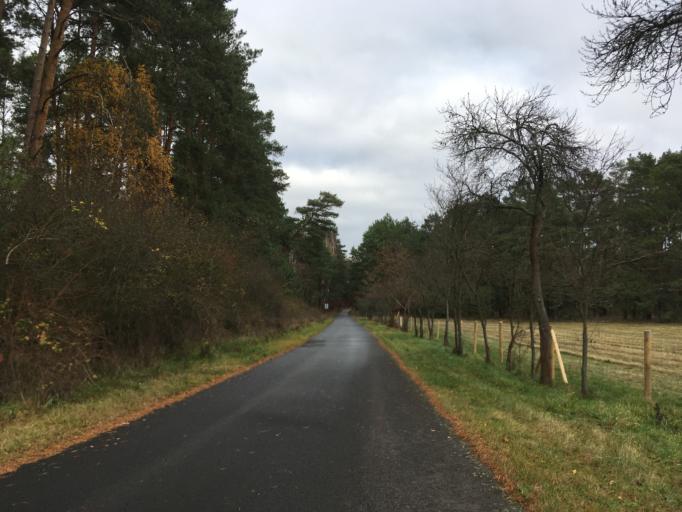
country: DE
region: Brandenburg
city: Jamlitz
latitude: 52.0311
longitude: 14.4681
